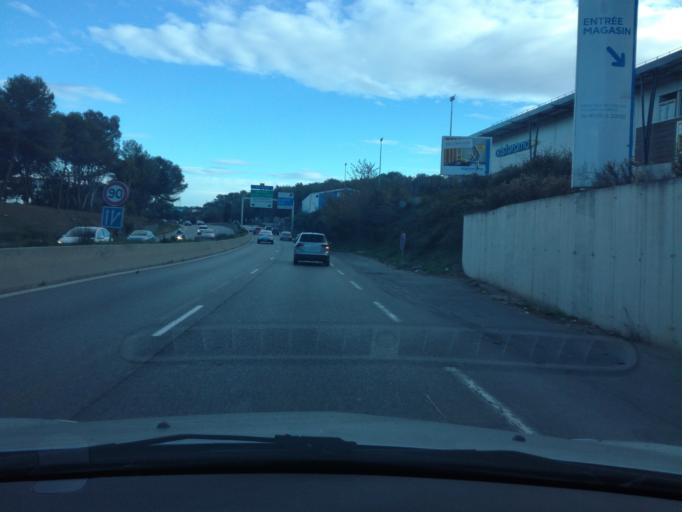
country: FR
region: Provence-Alpes-Cote d'Azur
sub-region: Departement des Alpes-Maritimes
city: Vallauris
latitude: 43.6031
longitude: 7.0702
